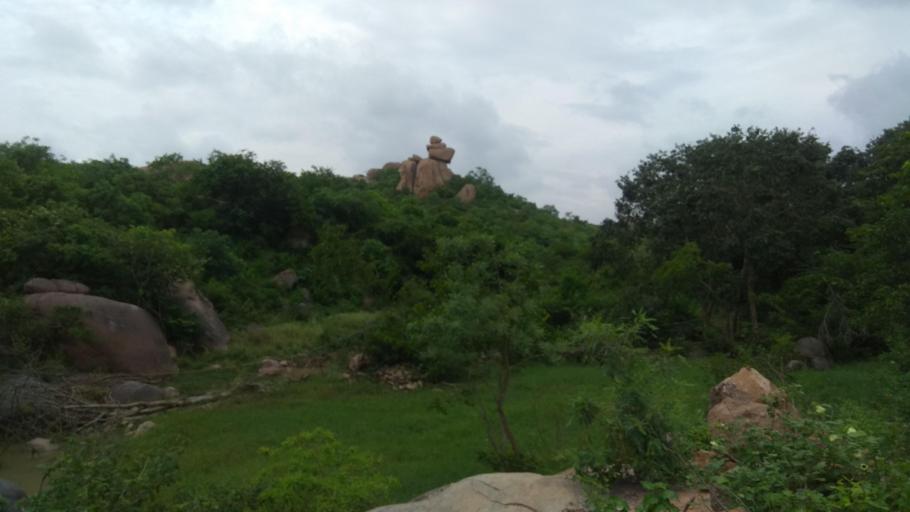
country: IN
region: Telangana
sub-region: Mahbubnagar
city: Farrukhnagar
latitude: 16.8943
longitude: 78.5004
